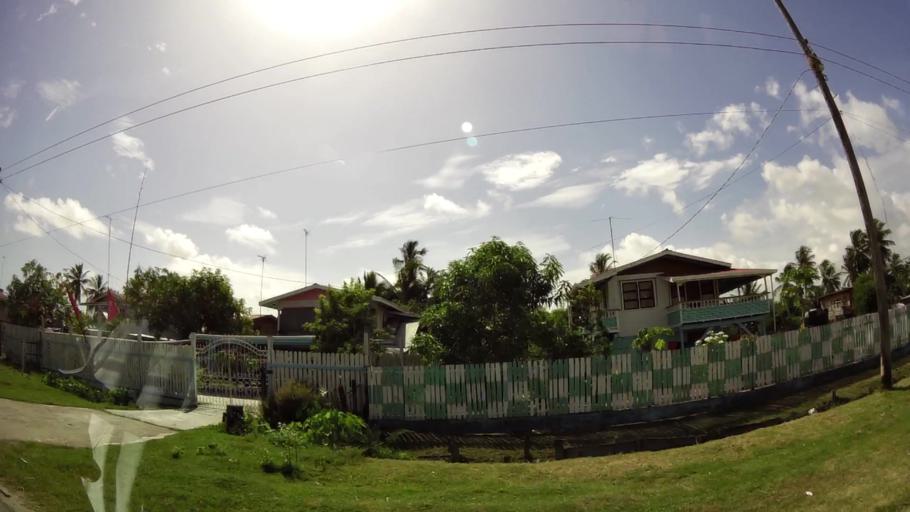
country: GY
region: Demerara-Mahaica
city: Mahaica Village
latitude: 6.7527
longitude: -57.9952
